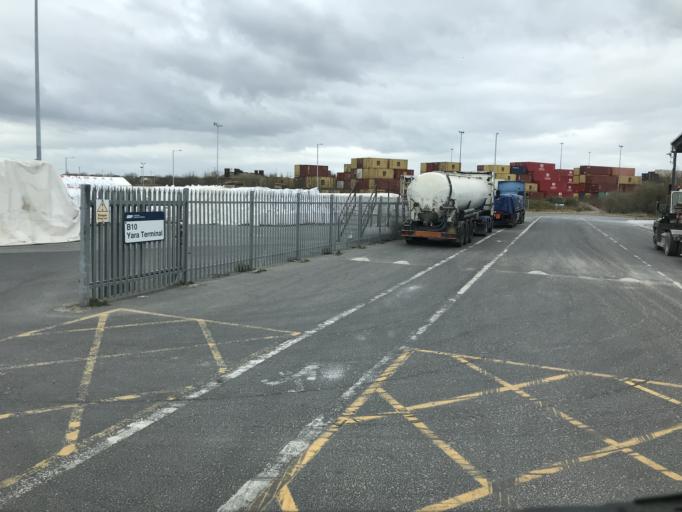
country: GB
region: England
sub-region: Cheshire West and Chester
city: Ellesmere Port
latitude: 53.3509
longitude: -2.9064
